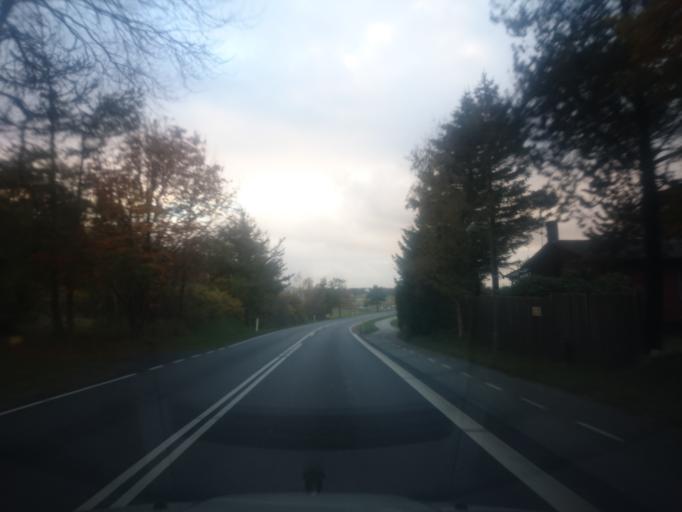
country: DK
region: South Denmark
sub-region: Billund Kommune
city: Billund
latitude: 55.7459
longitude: 9.1366
